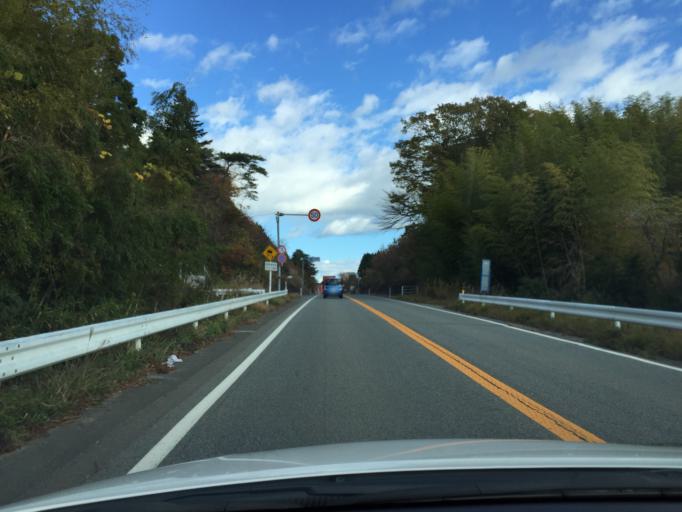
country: JP
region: Fukushima
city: Namie
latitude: 37.4296
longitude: 141.0082
